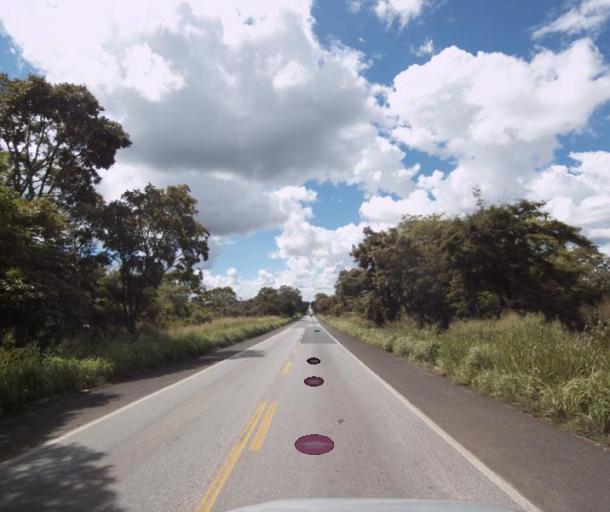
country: BR
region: Goias
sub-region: Porangatu
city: Porangatu
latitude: -13.8064
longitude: -49.0382
